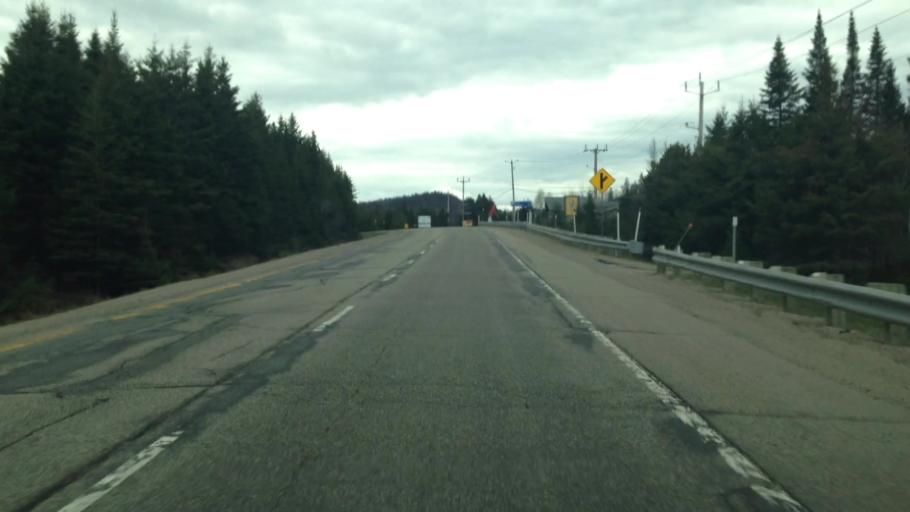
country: CA
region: Quebec
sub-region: Laurentides
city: Sainte-Agathe-des-Monts
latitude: 46.1043
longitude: -74.3975
